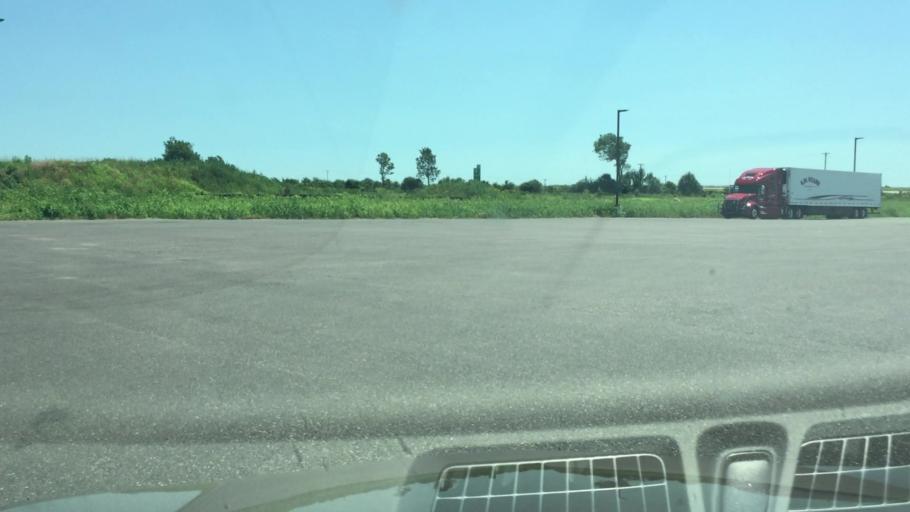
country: US
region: Wisconsin
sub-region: Fond du Lac County
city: Waupun
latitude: 43.6076
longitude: -88.7232
